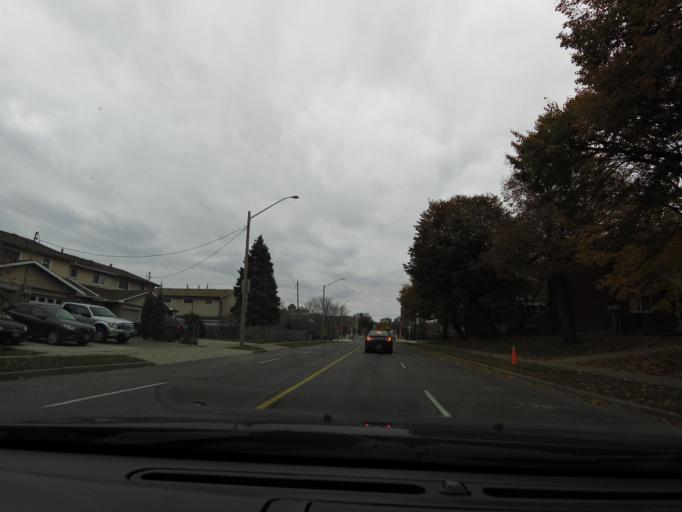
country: CA
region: Ontario
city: Hamilton
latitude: 43.2677
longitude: -79.8643
